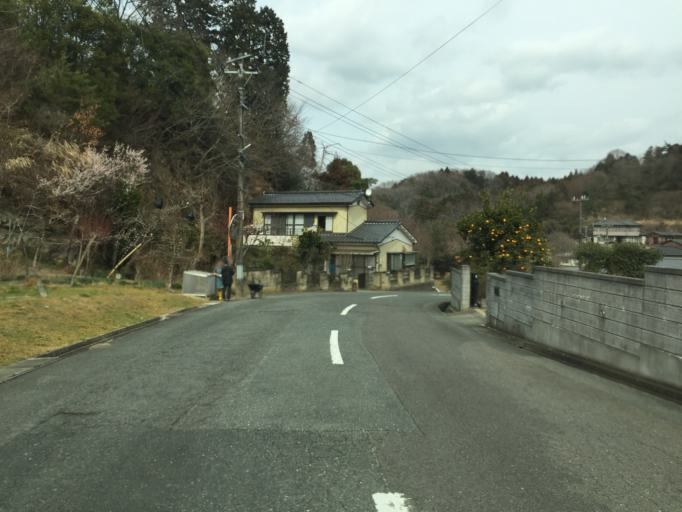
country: JP
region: Ibaraki
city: Kitaibaraki
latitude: 36.8742
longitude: 140.7836
